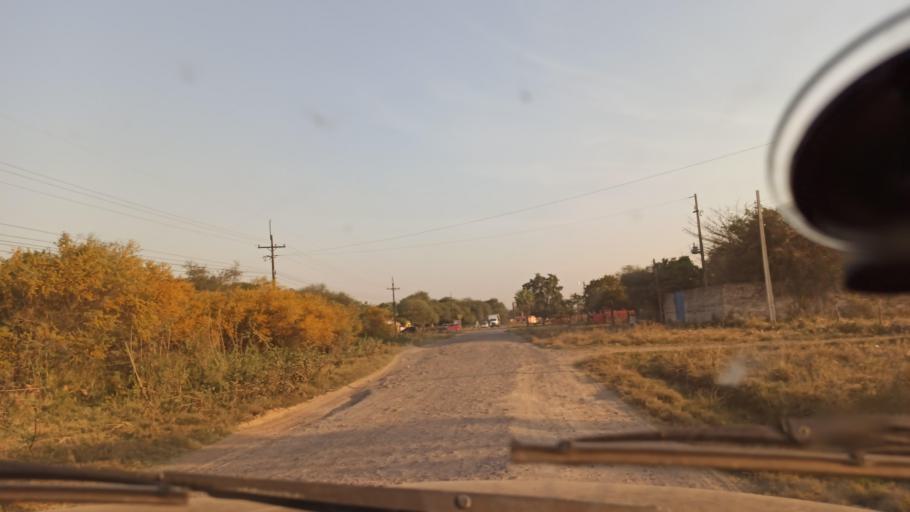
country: PY
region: Presidente Hayes
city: Nanawa
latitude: -25.2325
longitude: -57.6312
